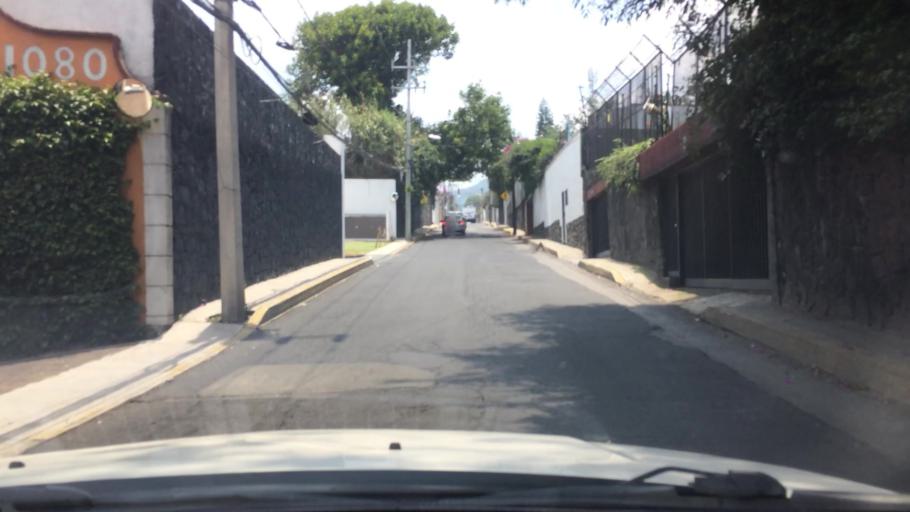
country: MX
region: Mexico City
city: Magdalena Contreras
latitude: 19.3254
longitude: -99.2215
